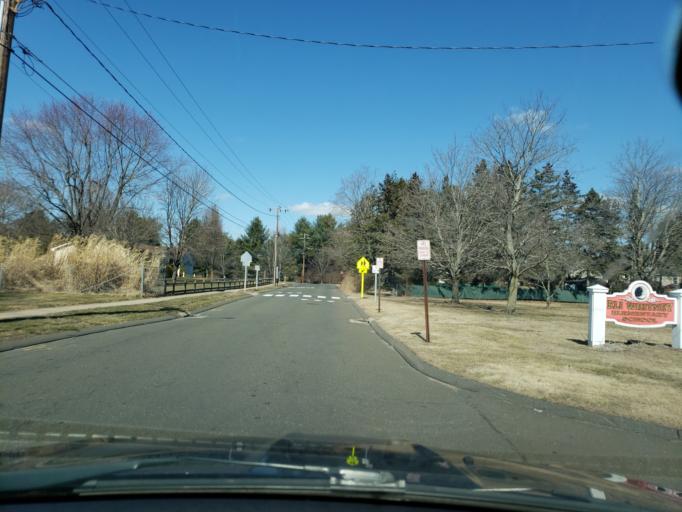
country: US
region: Connecticut
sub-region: Hartford County
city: Hazardville
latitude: 41.9842
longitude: -72.5585
